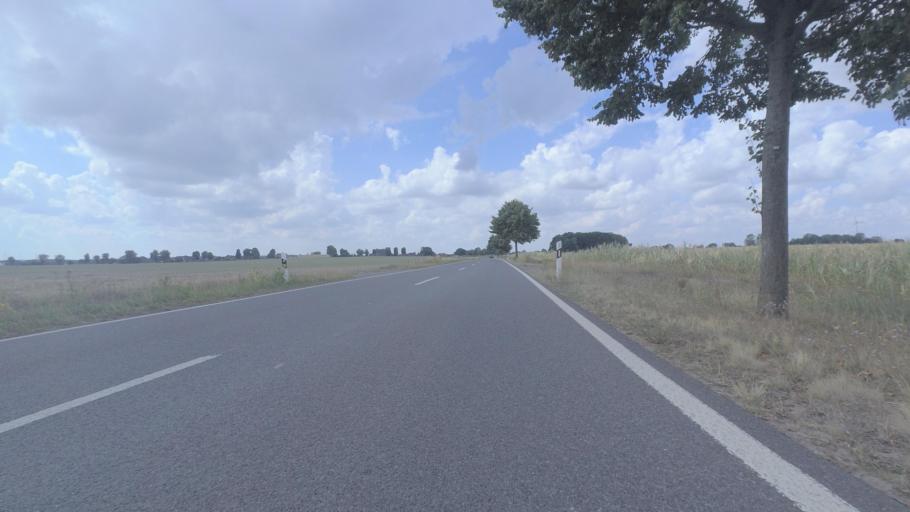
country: DE
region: Brandenburg
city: Wittstock
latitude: 53.1887
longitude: 12.4826
